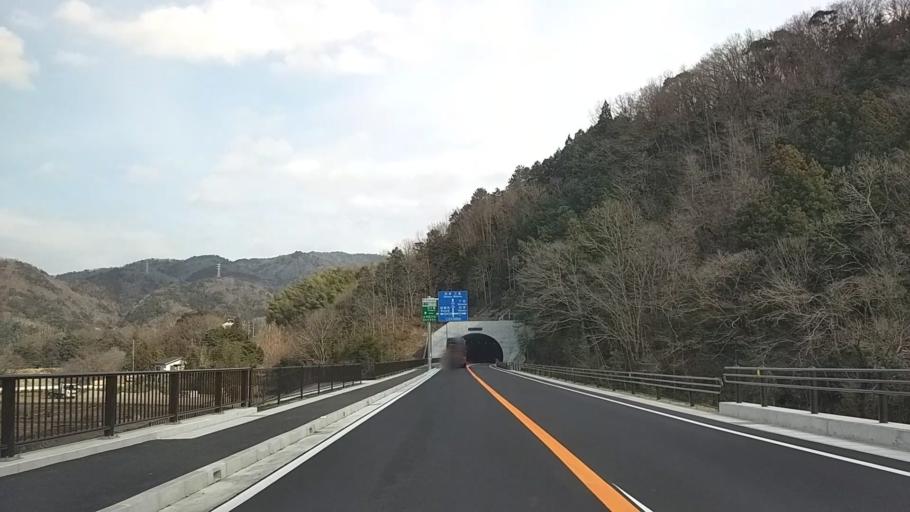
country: JP
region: Shizuoka
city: Heda
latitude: 34.9237
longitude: 138.9257
